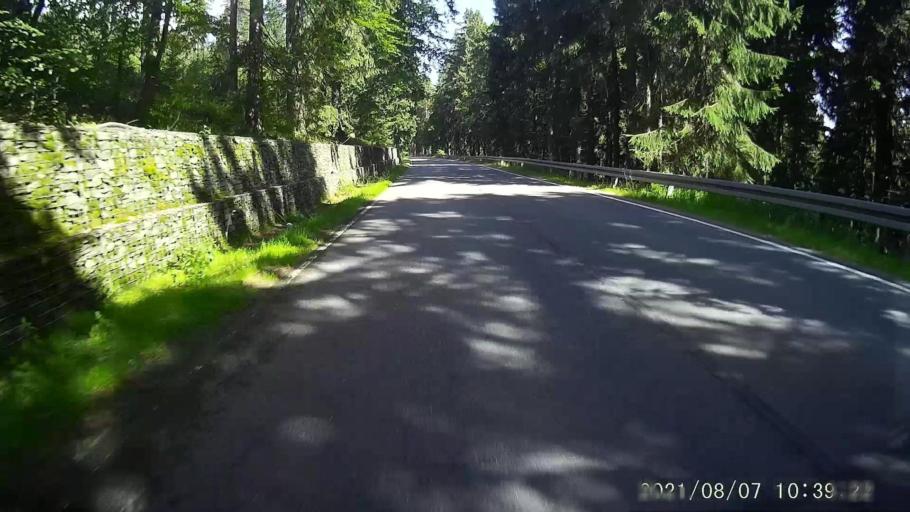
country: PL
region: Lower Silesian Voivodeship
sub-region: Powiat klodzki
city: Duszniki-Zdroj
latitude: 50.3496
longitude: 16.3789
